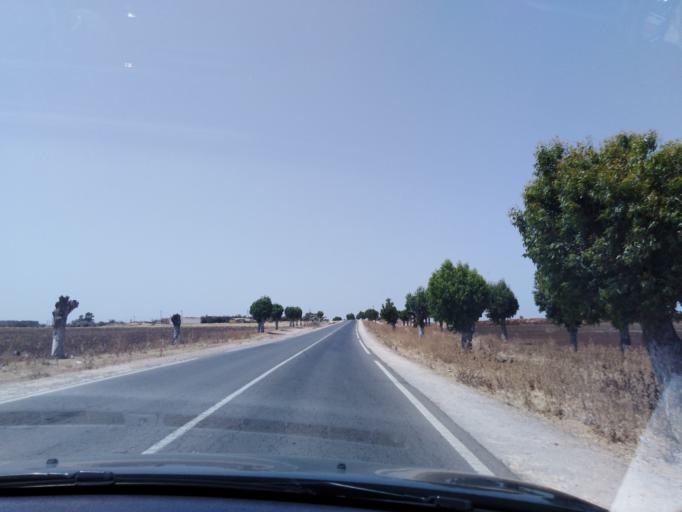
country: MA
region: Doukkala-Abda
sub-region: Safi
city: Youssoufia
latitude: 32.3783
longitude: -8.8275
